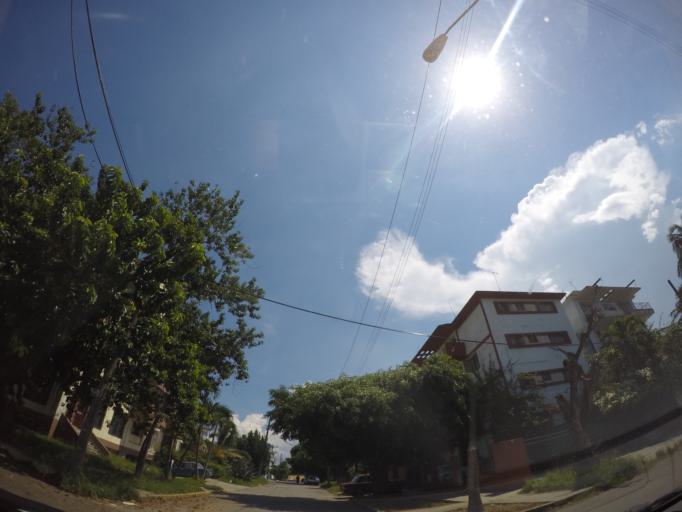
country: CU
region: La Habana
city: Havana
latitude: 23.1257
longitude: -82.4041
